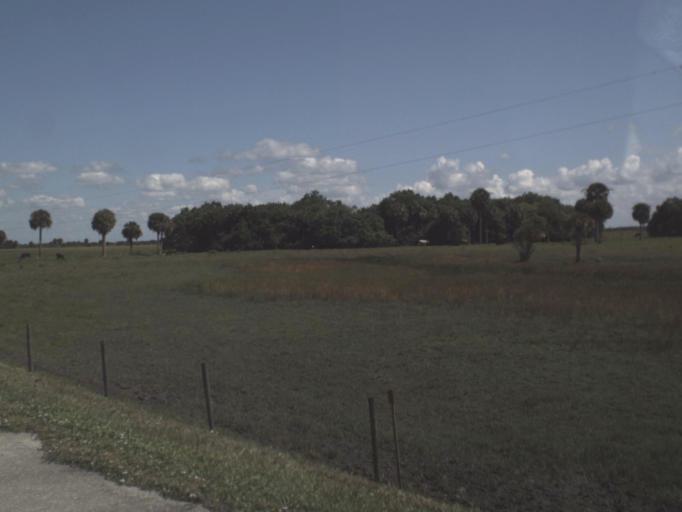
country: US
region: Florida
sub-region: Glades County
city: Buckhead Ridge
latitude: 27.0976
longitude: -80.9540
